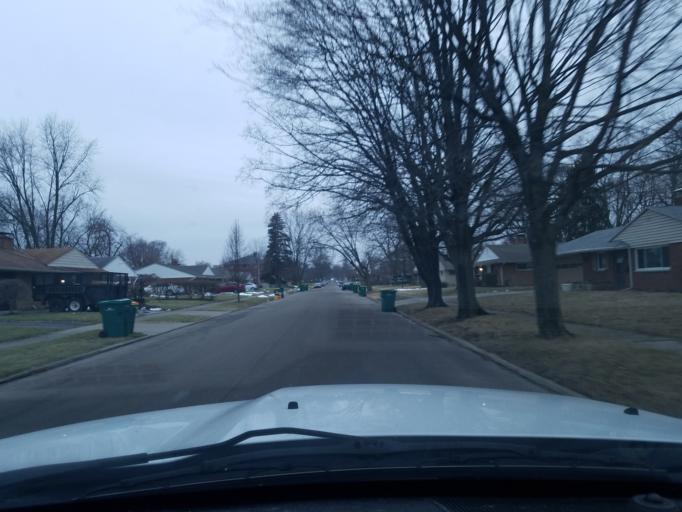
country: US
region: Ohio
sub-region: Montgomery County
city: Oakwood
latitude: 39.7135
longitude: -84.1565
